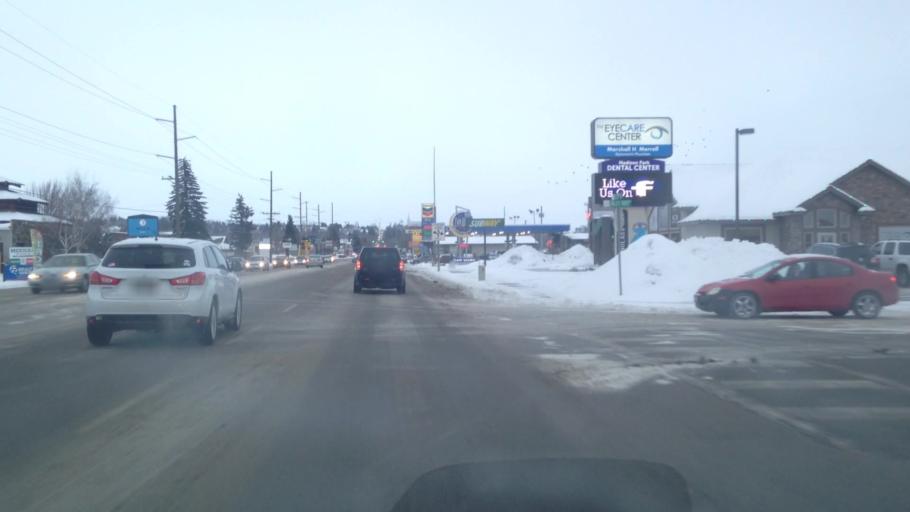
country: US
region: Idaho
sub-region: Madison County
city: Rexburg
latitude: 43.8334
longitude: -111.7782
